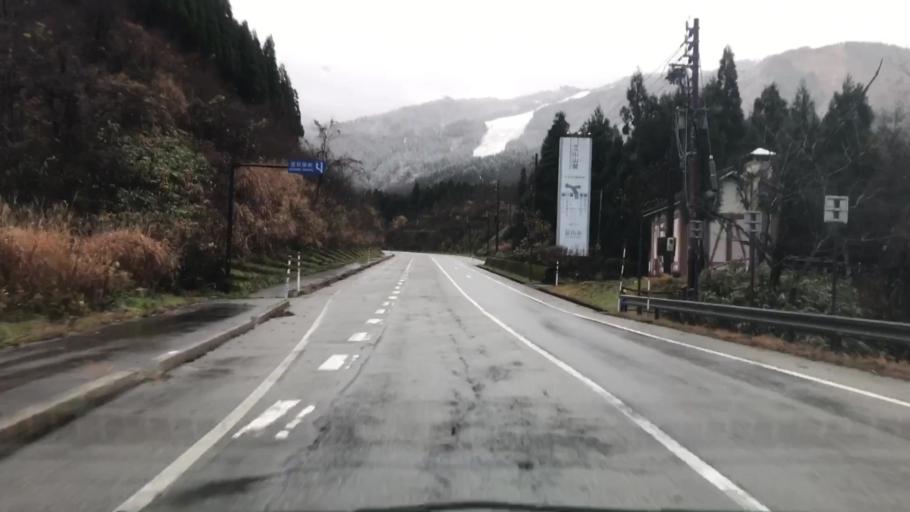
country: JP
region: Toyama
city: Kamiichi
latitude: 36.5789
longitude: 137.4075
